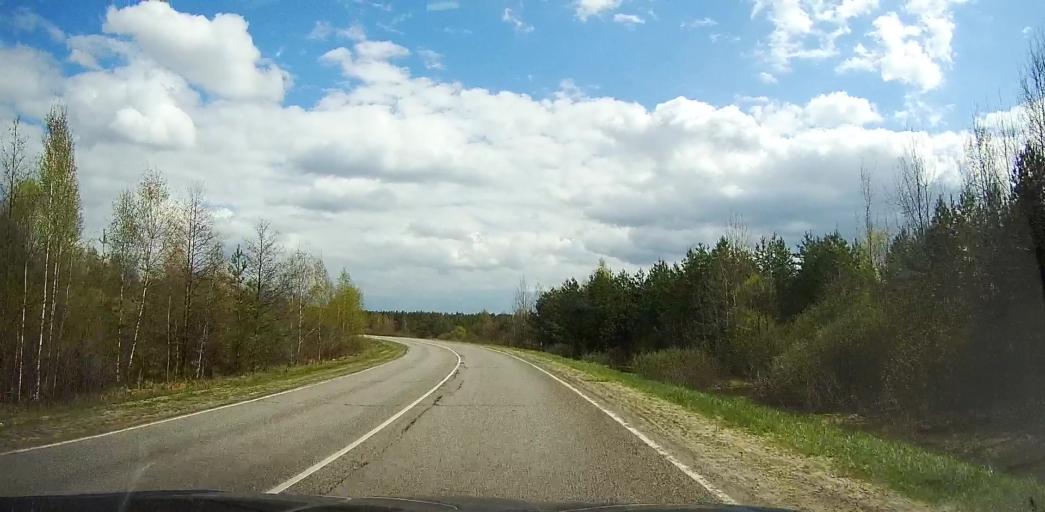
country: RU
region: Moskovskaya
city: Davydovo
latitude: 55.5475
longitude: 38.8109
